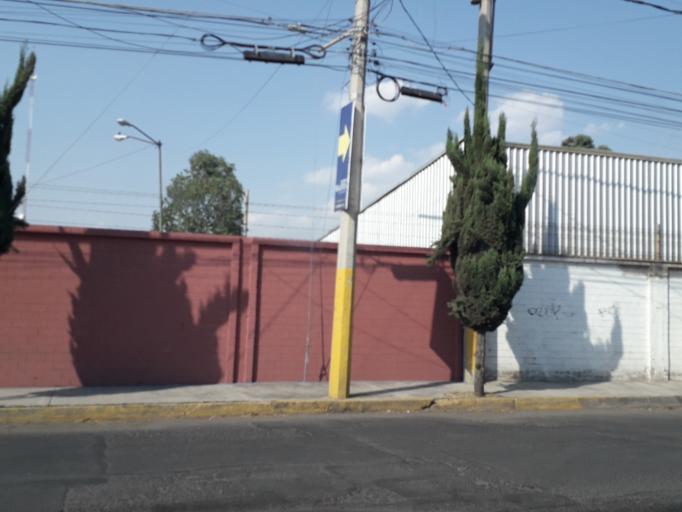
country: MX
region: Puebla
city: Puebla
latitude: 19.0157
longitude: -98.2111
